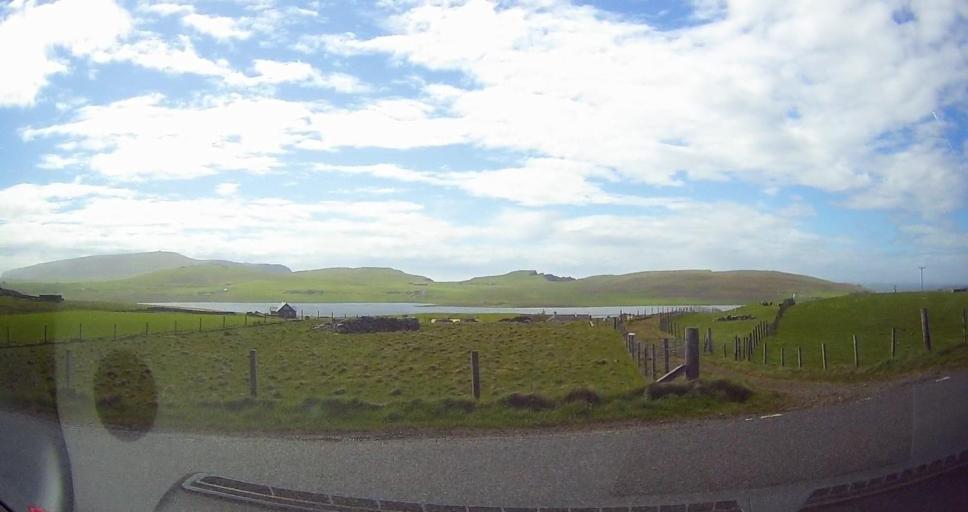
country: GB
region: Scotland
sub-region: Shetland Islands
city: Sandwick
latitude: 59.9384
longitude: -1.3218
